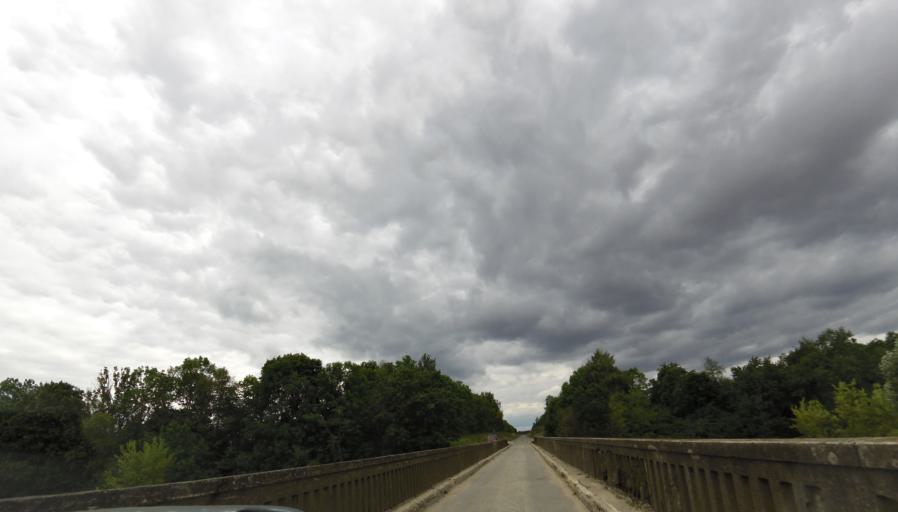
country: LT
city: Linkuva
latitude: 56.0579
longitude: 24.1621
